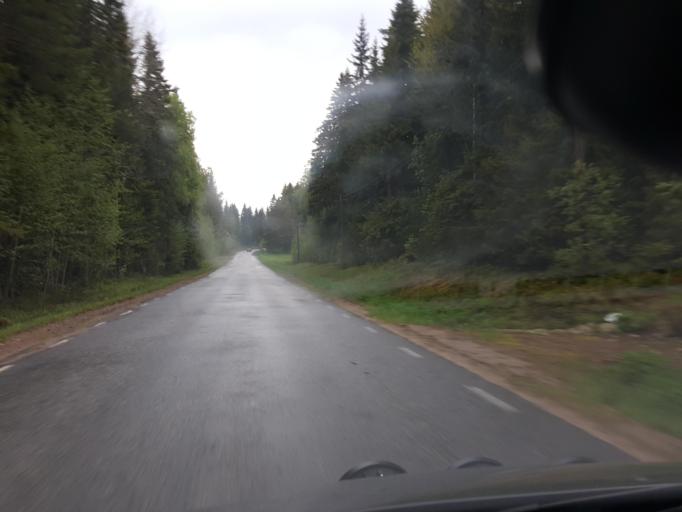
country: SE
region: Gaevleborg
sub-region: Ljusdals Kommun
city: Jaervsoe
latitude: 61.7388
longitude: 16.1913
